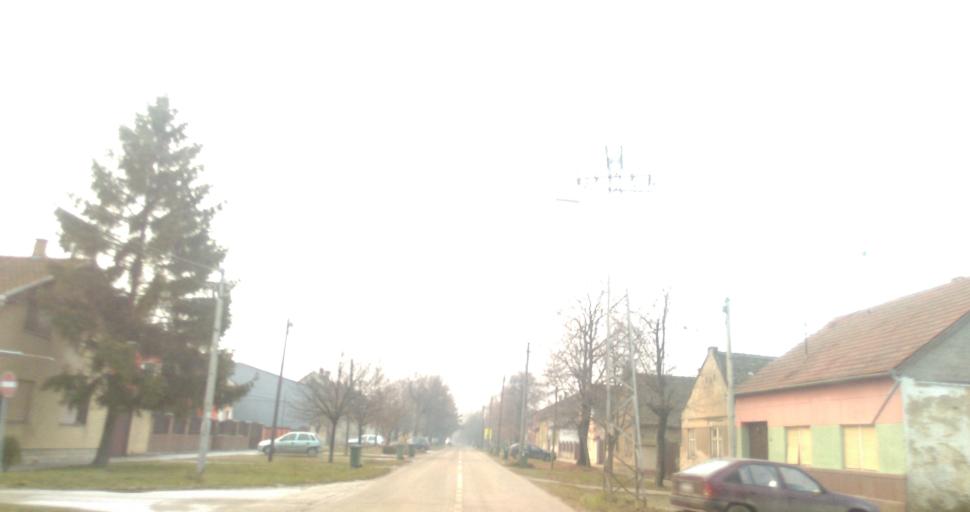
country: RS
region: Autonomna Pokrajina Vojvodina
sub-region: Juznobacki Okrug
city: Becej
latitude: 45.6090
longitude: 20.0443
